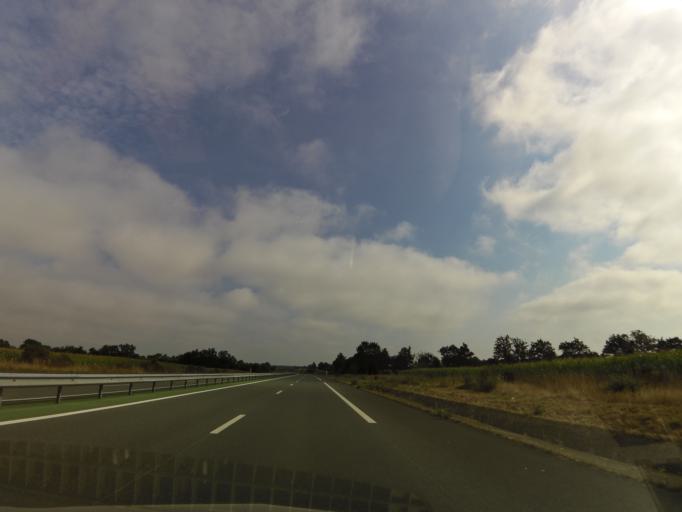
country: FR
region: Pays de la Loire
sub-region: Departement de la Vendee
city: La Ferriere
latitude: 46.7088
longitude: -1.2863
